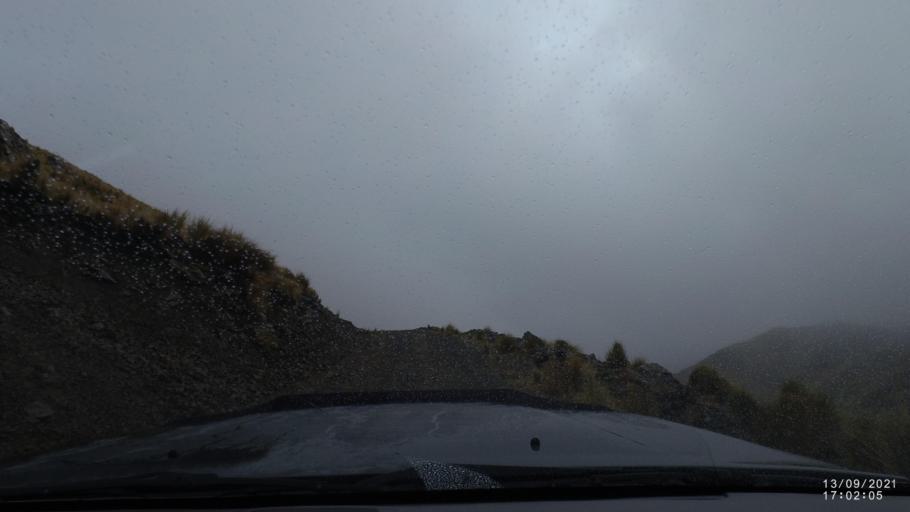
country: BO
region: Cochabamba
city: Colomi
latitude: -17.3162
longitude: -65.7218
